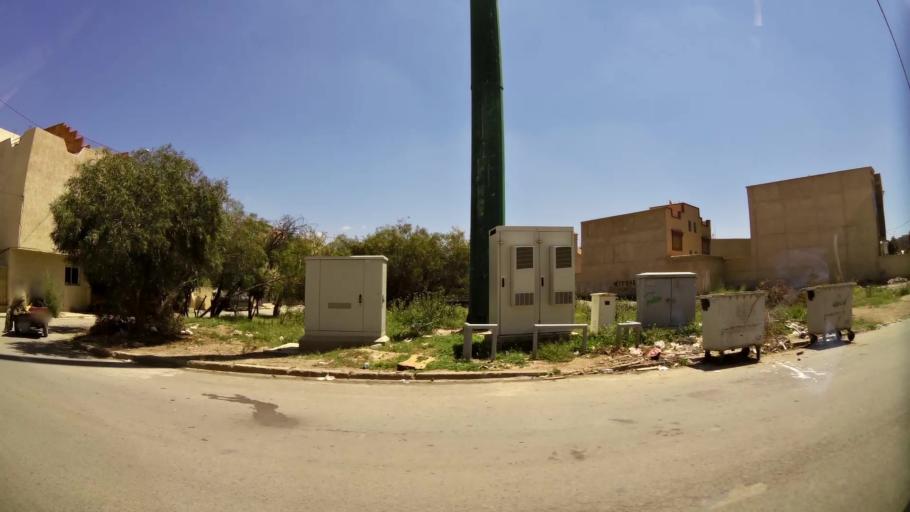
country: MA
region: Oriental
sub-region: Oujda-Angad
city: Oujda
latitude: 34.6583
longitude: -1.9424
